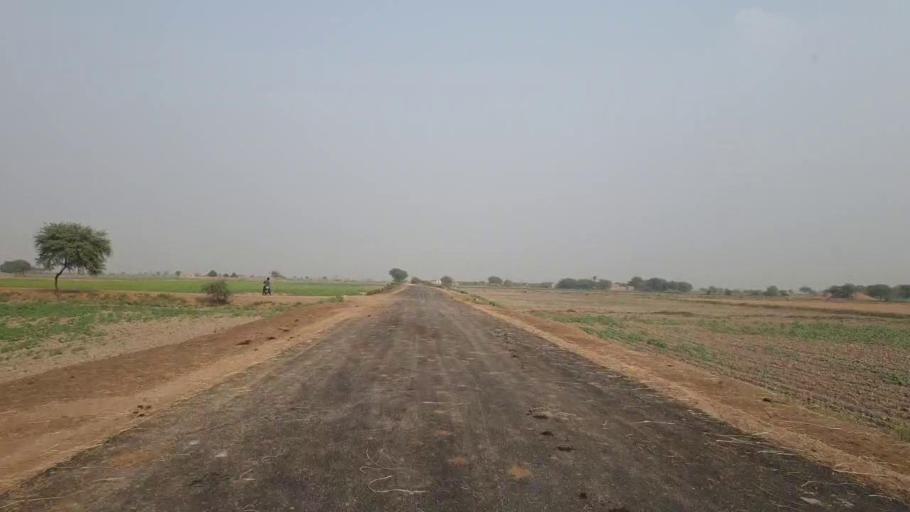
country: PK
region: Sindh
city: Mirpur Batoro
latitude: 24.5905
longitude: 68.4029
